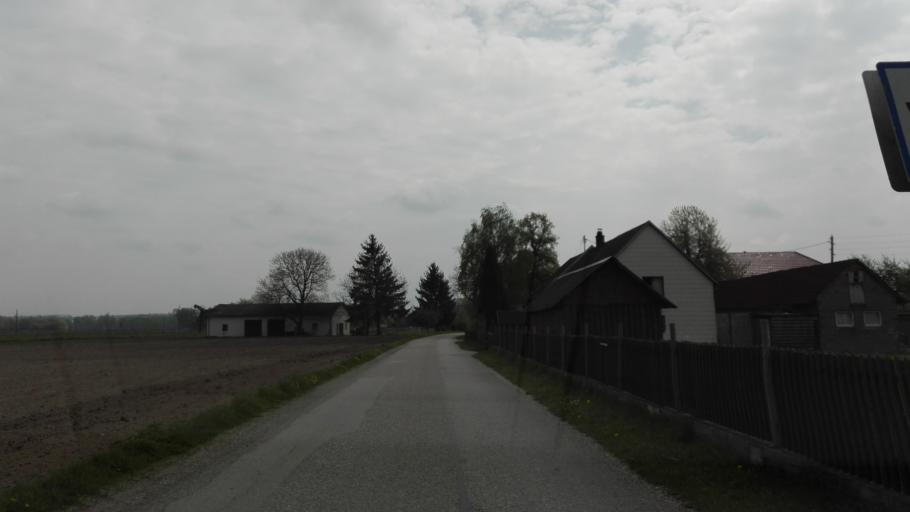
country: AT
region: Lower Austria
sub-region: Politischer Bezirk Amstetten
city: Strengberg
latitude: 48.1827
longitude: 14.6798
